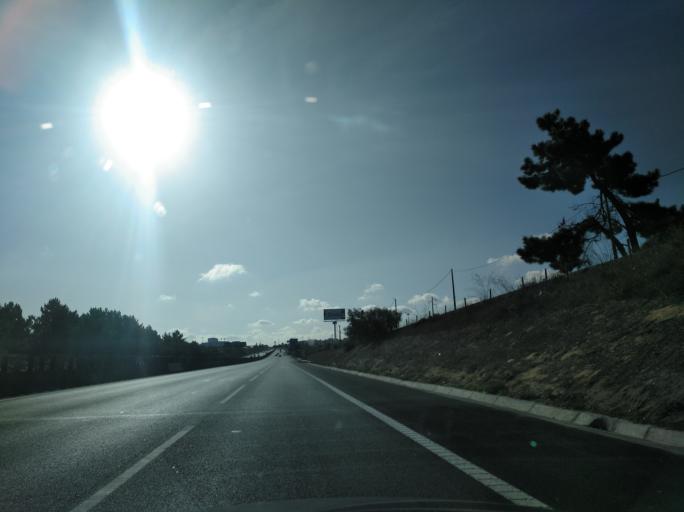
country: PT
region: Setubal
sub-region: Seixal
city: Corroios
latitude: 38.6262
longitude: -9.1380
